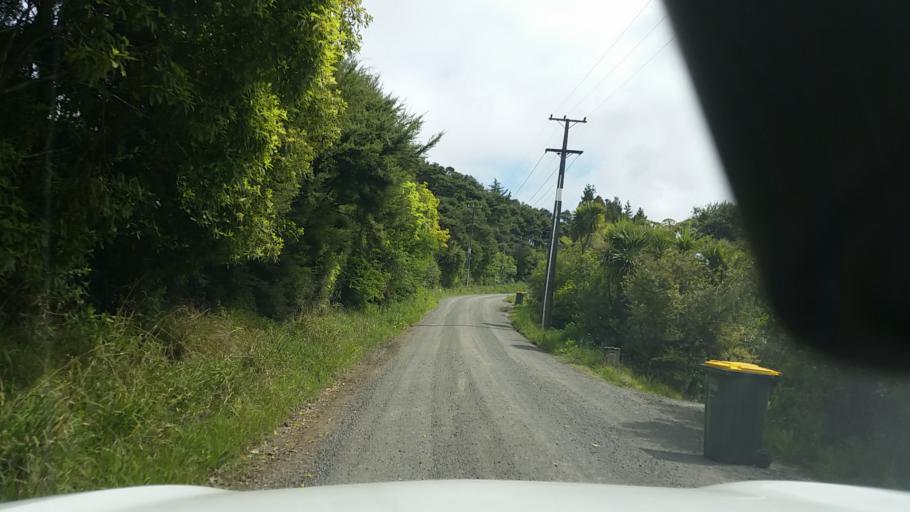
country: NZ
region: Auckland
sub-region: Auckland
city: Muriwai Beach
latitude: -36.8502
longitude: 174.5234
